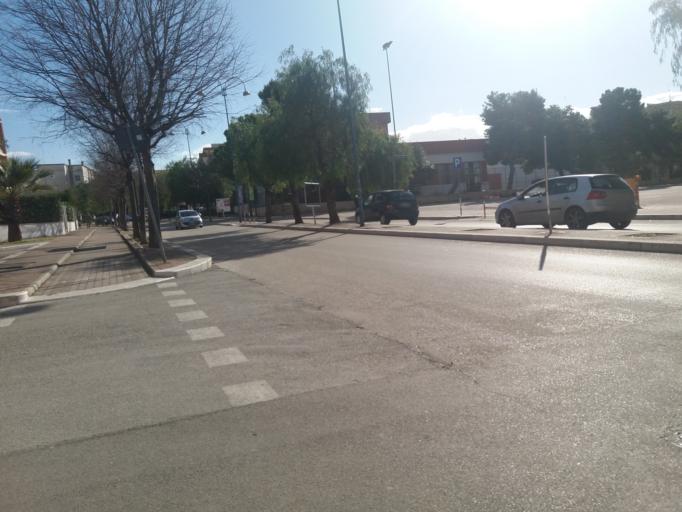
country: IT
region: Apulia
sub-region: Provincia di Barletta - Andria - Trani
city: Andria
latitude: 41.2337
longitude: 16.3016
